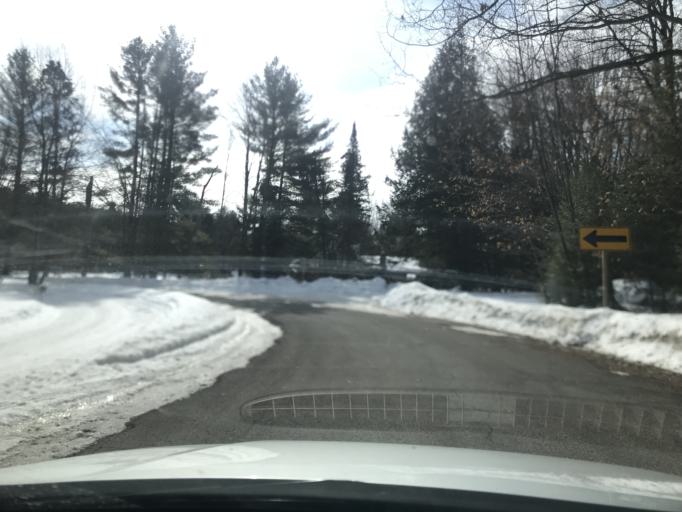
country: US
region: Wisconsin
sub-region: Menominee County
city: Legend Lake
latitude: 45.1061
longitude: -88.4332
